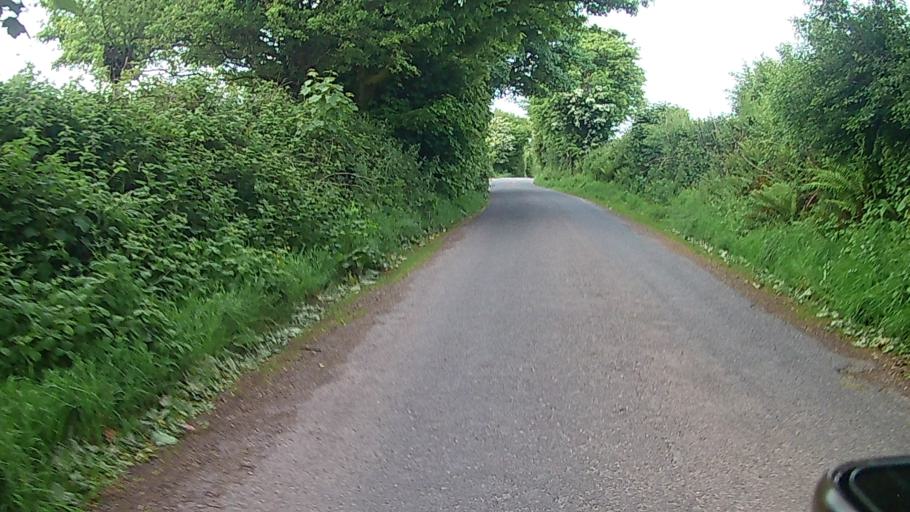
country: IE
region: Munster
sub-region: County Cork
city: Watergrasshill
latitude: 51.9836
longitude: -8.4065
